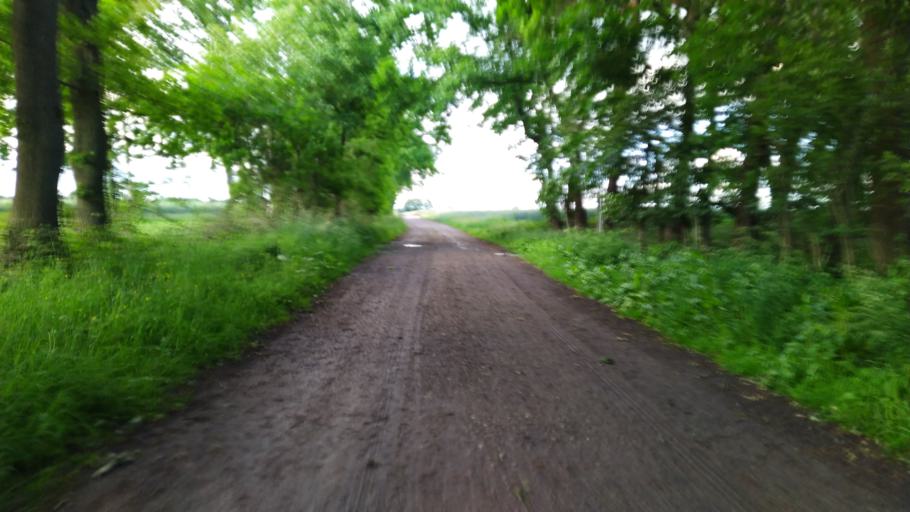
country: DE
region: Lower Saxony
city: Kutenholz
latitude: 53.4563
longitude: 9.3440
